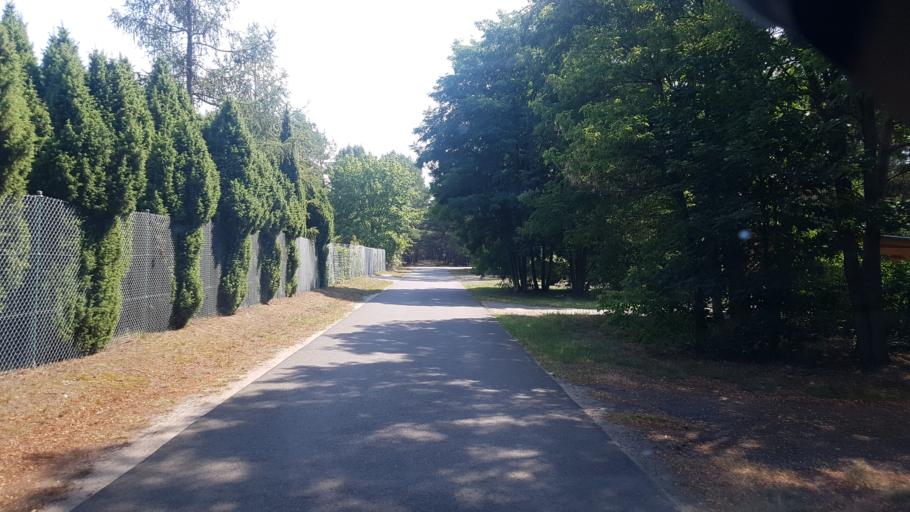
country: DE
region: Brandenburg
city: Spremberg
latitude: 51.6316
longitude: 14.4038
